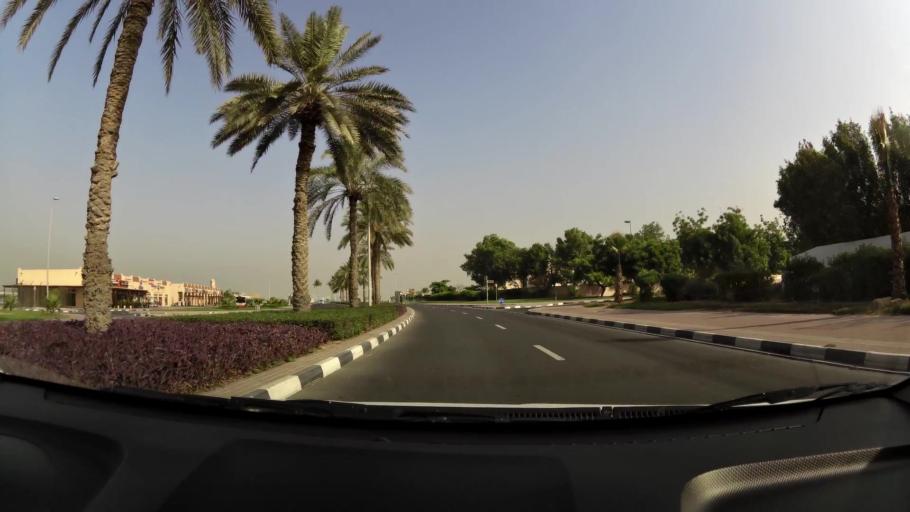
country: AE
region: Ash Shariqah
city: Sharjah
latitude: 25.3080
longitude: 55.3406
